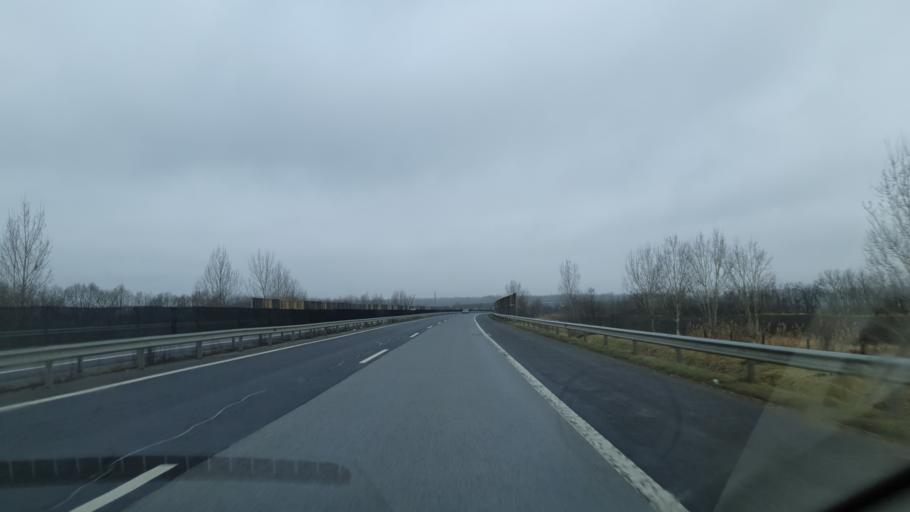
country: HU
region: Hajdu-Bihar
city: Polgar
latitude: 47.8474
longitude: 21.0823
